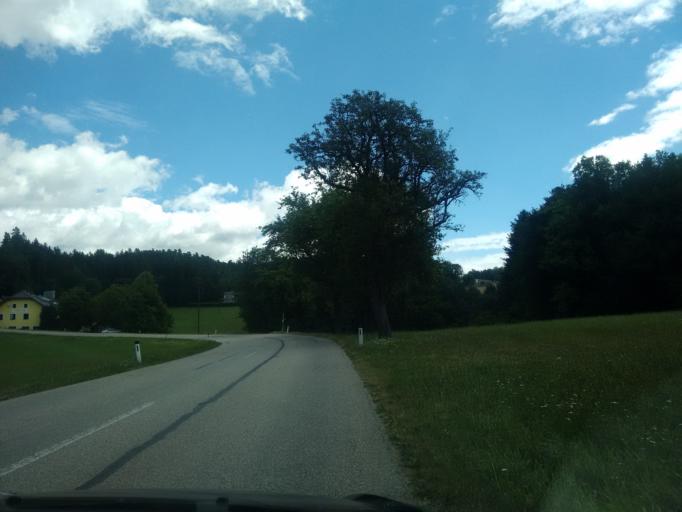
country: AT
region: Upper Austria
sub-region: Politischer Bezirk Urfahr-Umgebung
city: Walding
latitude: 48.3652
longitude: 14.1650
